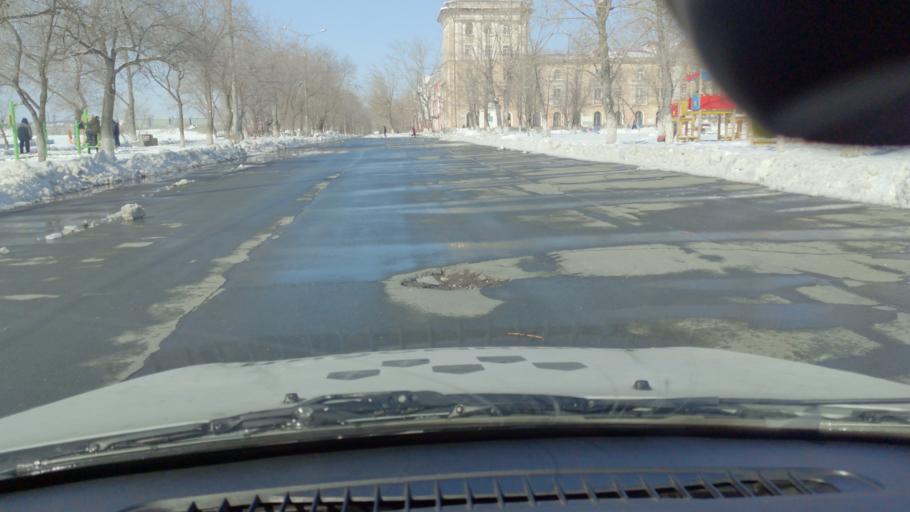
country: RU
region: Samara
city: Zhigulevsk
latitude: 53.4635
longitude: 49.5327
